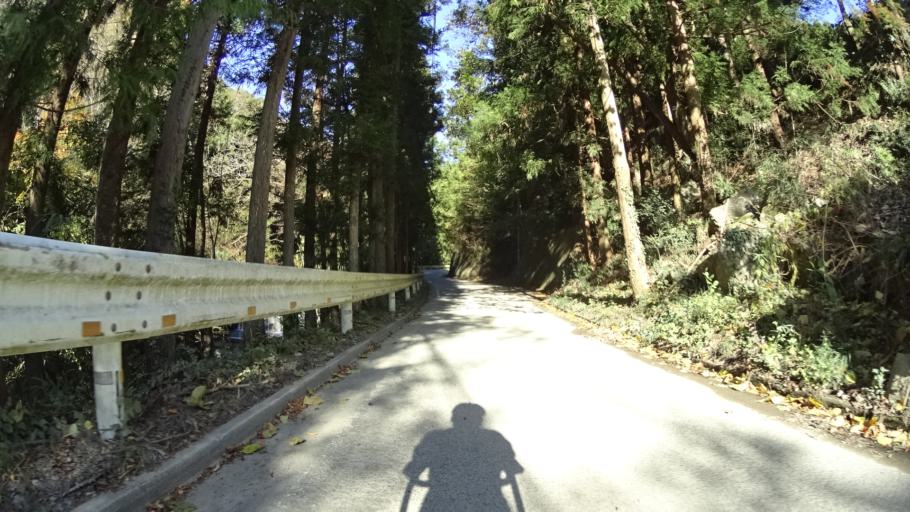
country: JP
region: Yamanashi
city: Uenohara
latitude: 35.6409
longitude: 139.1394
